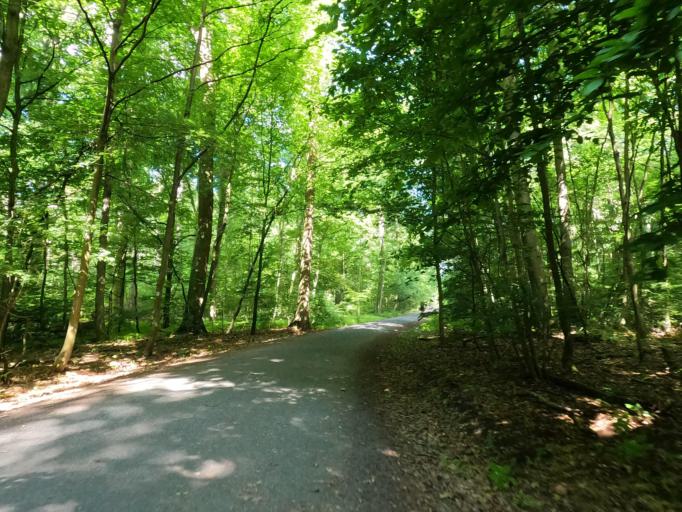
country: DE
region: Hesse
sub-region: Regierungsbezirk Darmstadt
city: Neu Isenburg
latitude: 50.0856
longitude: 8.7146
